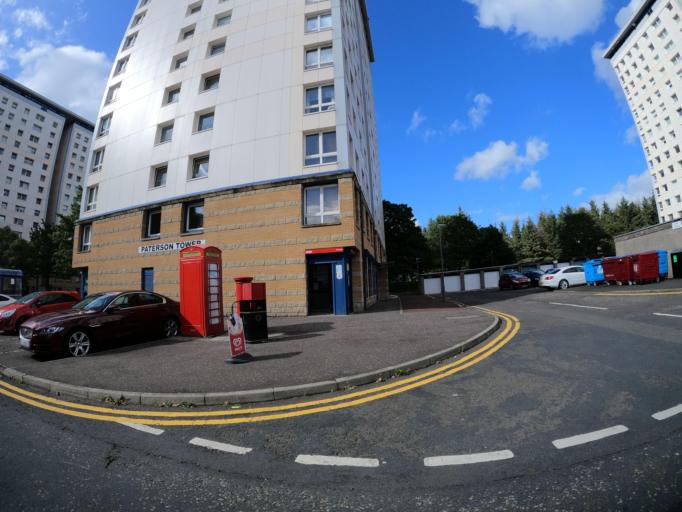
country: GB
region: Scotland
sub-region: Falkirk
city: Falkirk
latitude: 55.9964
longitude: -3.7715
